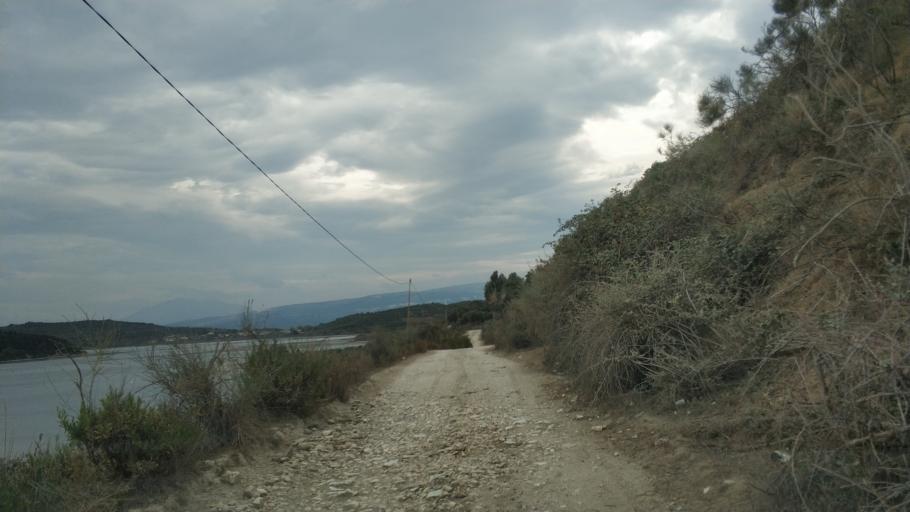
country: AL
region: Vlore
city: Vlore
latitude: 40.5192
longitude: 19.3914
